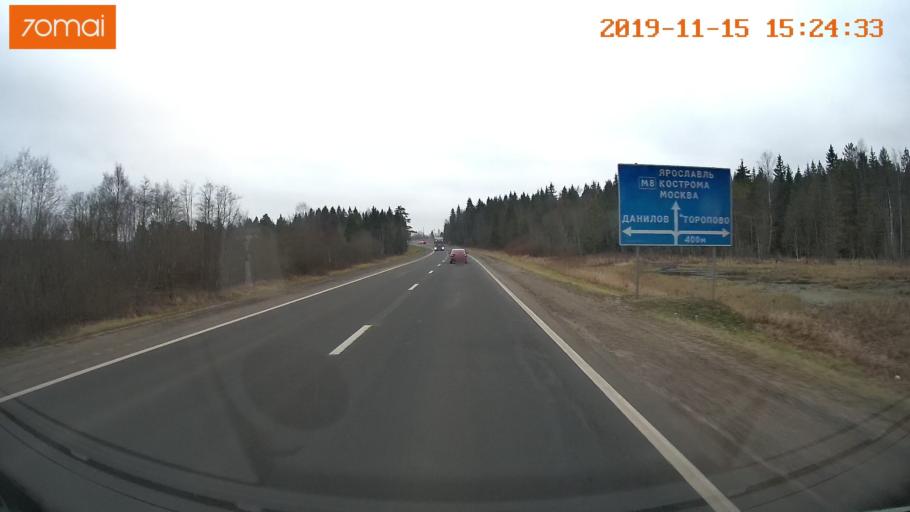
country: RU
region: Jaroslavl
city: Danilov
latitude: 58.1762
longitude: 40.1330
